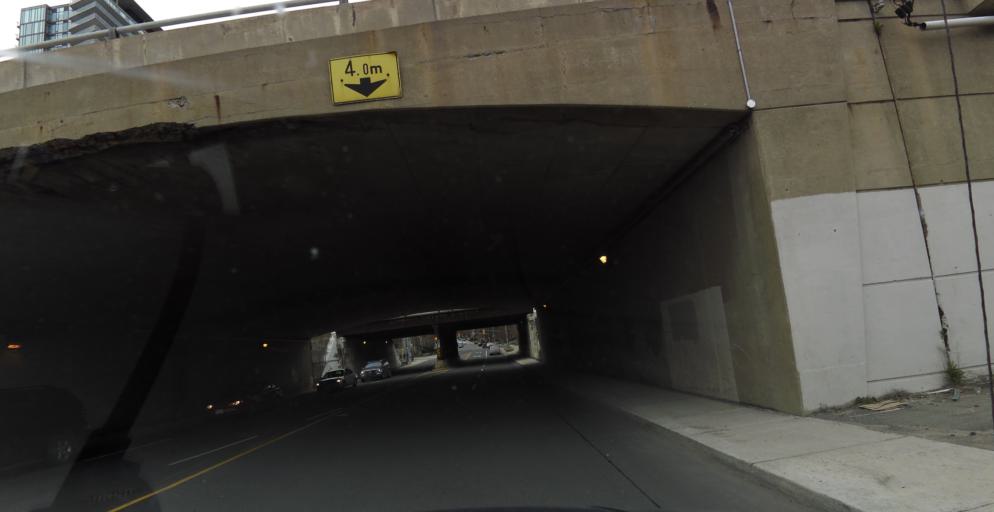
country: CA
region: Ontario
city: Toronto
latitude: 43.6355
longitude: -79.4684
